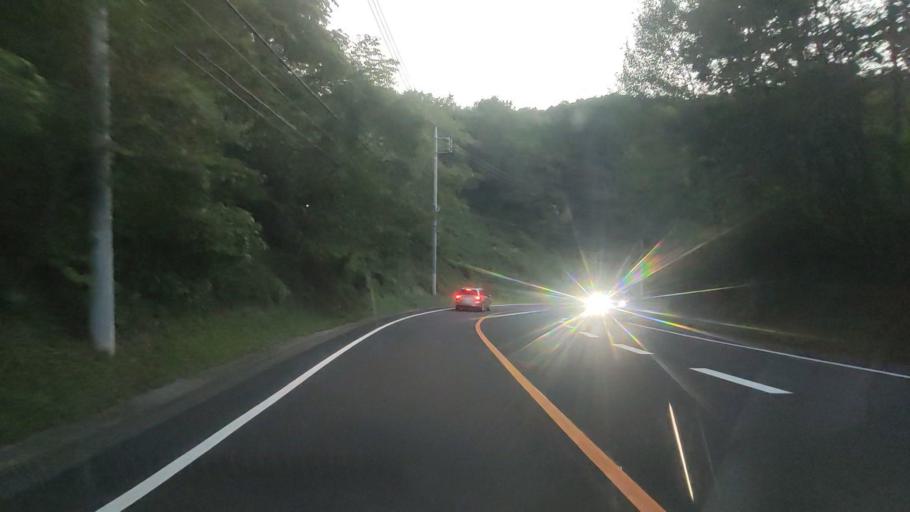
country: JP
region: Gunma
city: Nakanojomachi
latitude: 36.5398
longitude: 138.6113
